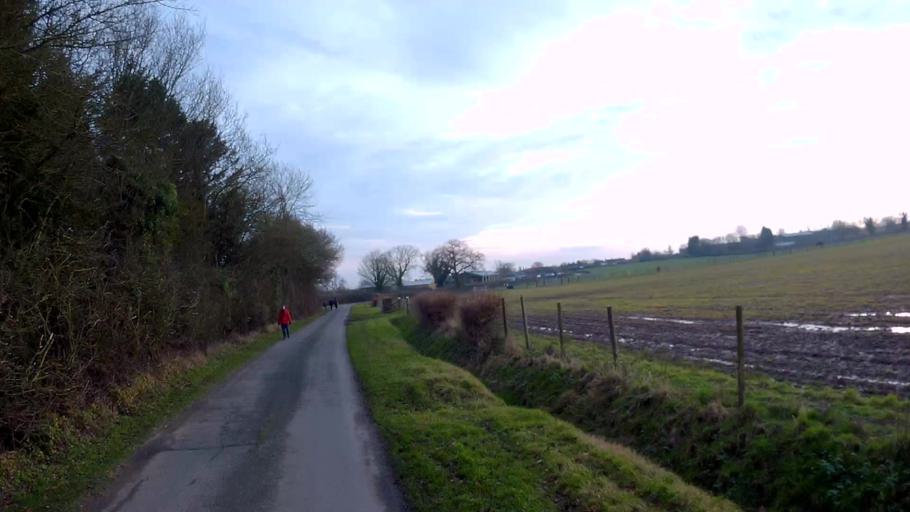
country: GB
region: England
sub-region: Lincolnshire
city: Bourne
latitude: 52.8174
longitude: -0.3994
